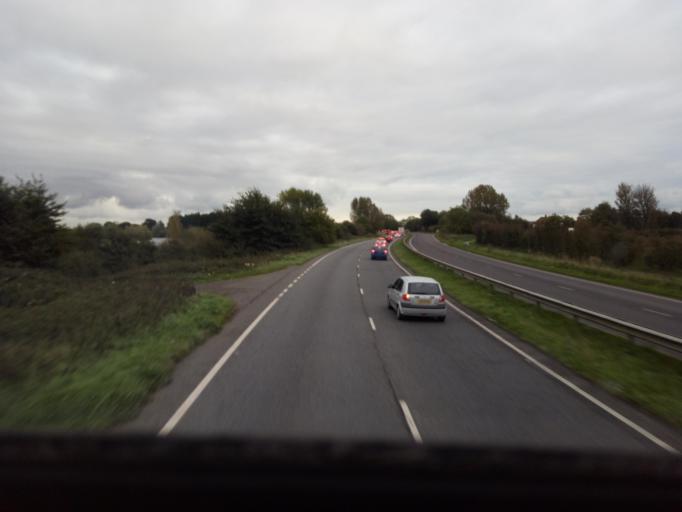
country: GB
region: England
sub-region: West Sussex
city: Chichester
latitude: 50.8294
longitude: -0.7436
